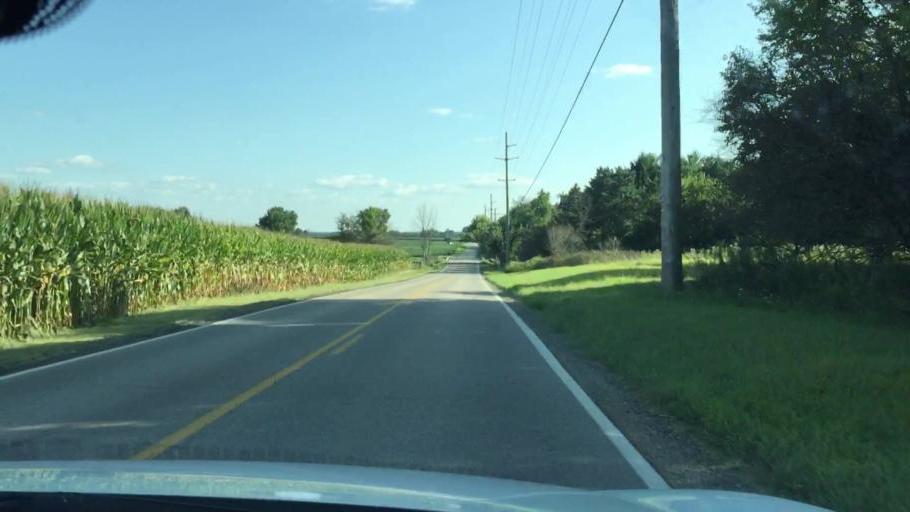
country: US
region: Ohio
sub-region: Clark County
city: Northridge
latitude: 39.9518
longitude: -83.7092
